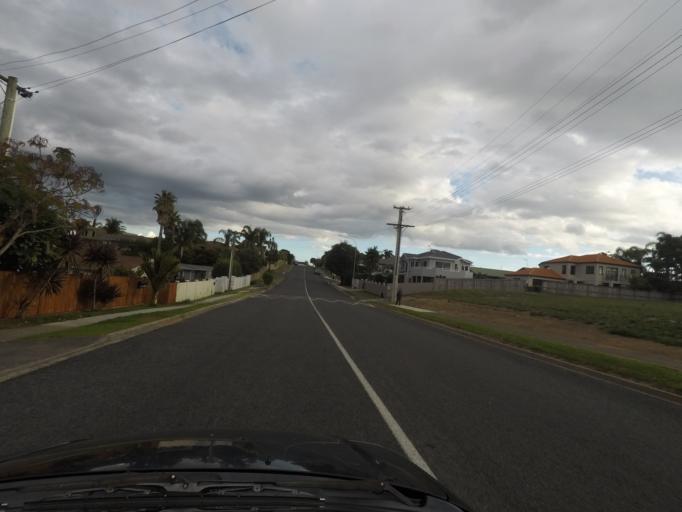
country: NZ
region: Auckland
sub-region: Auckland
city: Rosebank
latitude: -36.8023
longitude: 174.6453
